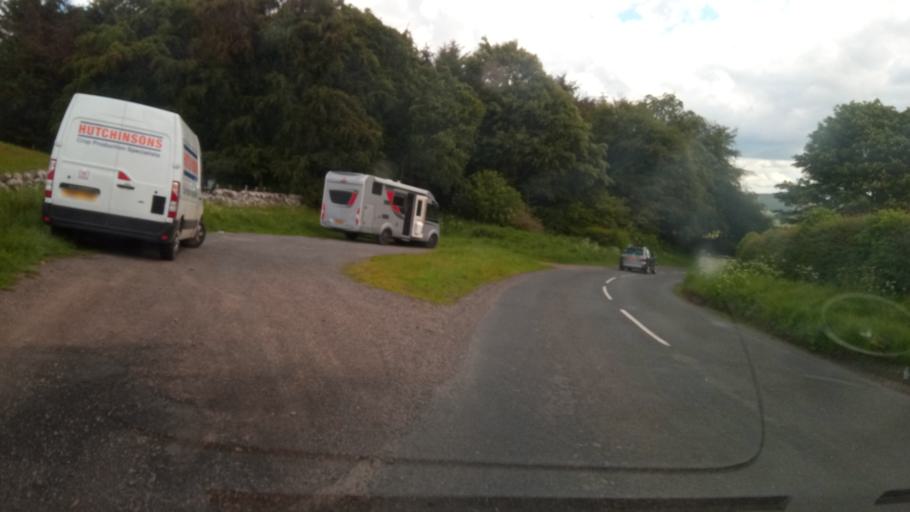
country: GB
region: Scotland
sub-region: The Scottish Borders
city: Coldstream
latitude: 55.6039
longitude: -2.2585
